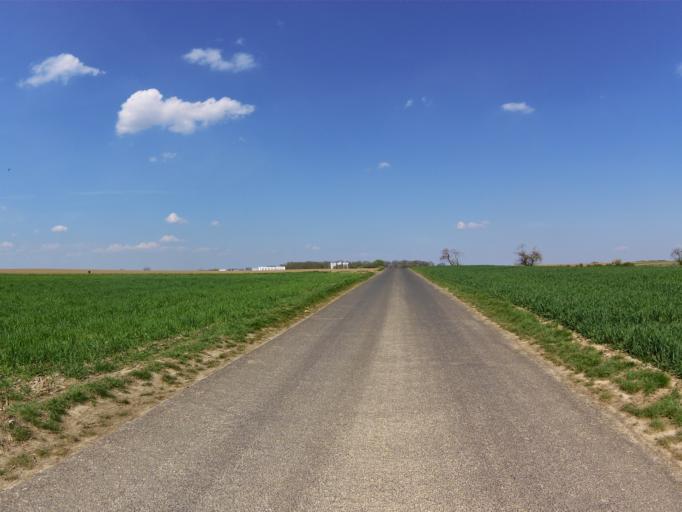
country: DE
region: Bavaria
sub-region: Regierungsbezirk Unterfranken
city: Giebelstadt
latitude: 49.6763
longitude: 9.9517
